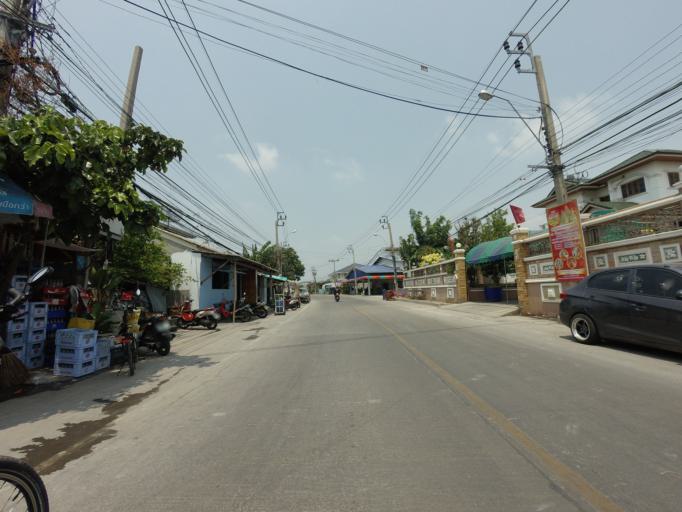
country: TH
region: Samut Prakan
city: Phra Samut Chedi
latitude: 13.5715
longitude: 100.5697
